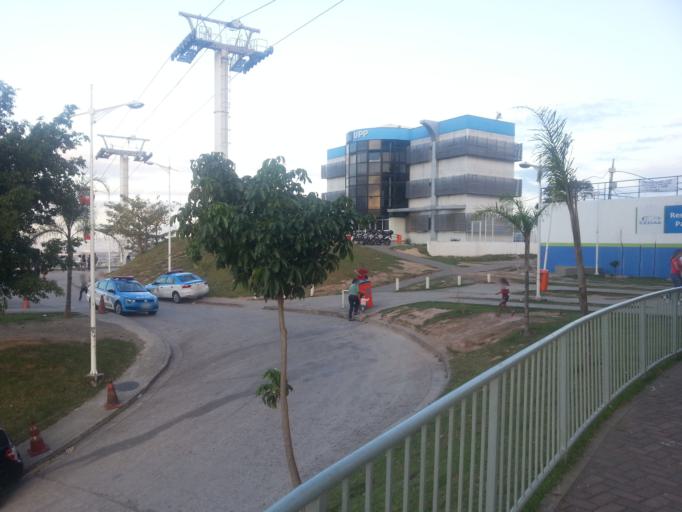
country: BR
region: Rio de Janeiro
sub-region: Duque De Caxias
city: Duque de Caxias
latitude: -22.8628
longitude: -43.2814
